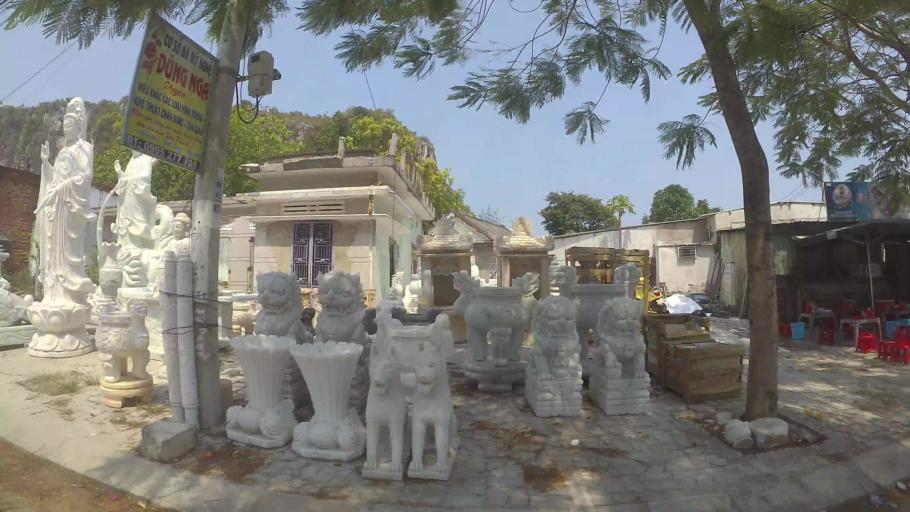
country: VN
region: Da Nang
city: Ngu Hanh Son
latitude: 15.9989
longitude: 108.2613
